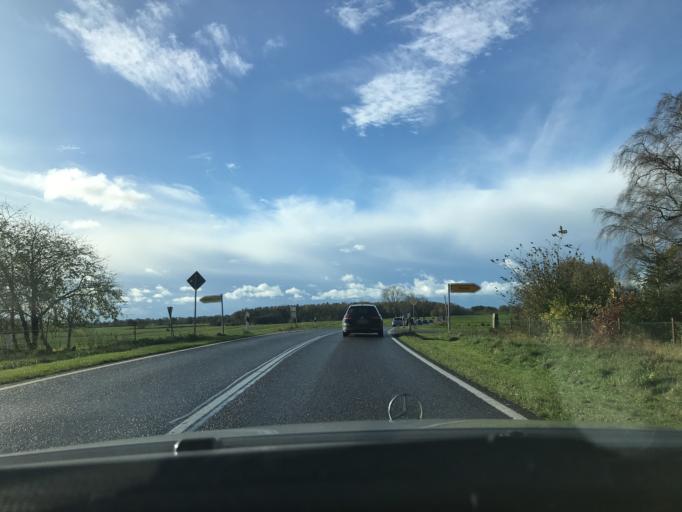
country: DE
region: Mecklenburg-Vorpommern
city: Zussow
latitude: 53.9680
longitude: 13.5351
